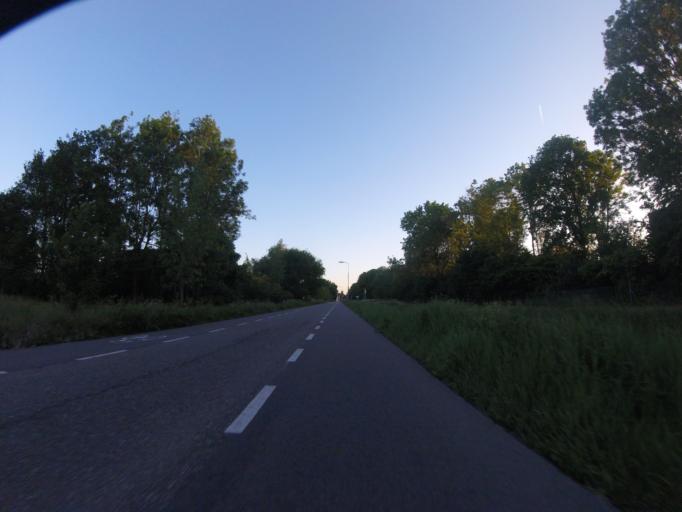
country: NL
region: North Holland
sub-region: Gemeente Heemstede
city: Heemstede
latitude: 52.3330
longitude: 4.6527
